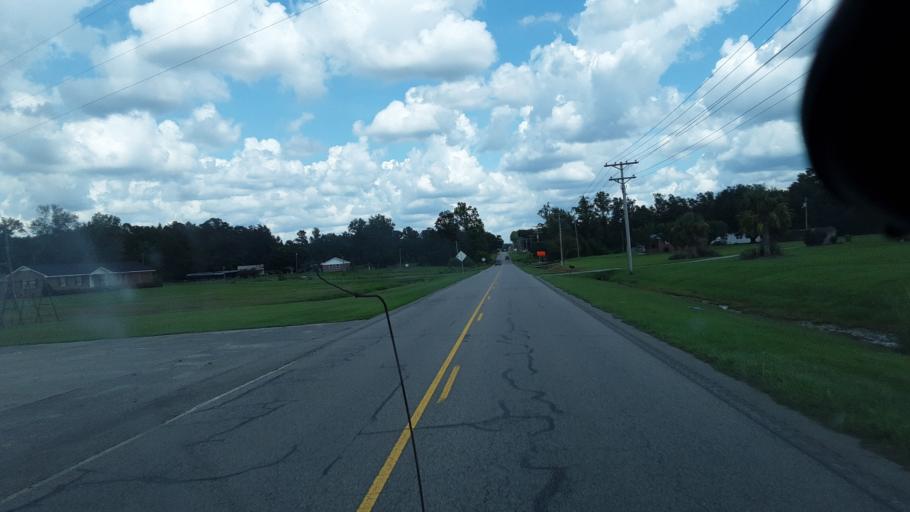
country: US
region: South Carolina
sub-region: Williamsburg County
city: Andrews
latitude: 33.5050
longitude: -79.5213
